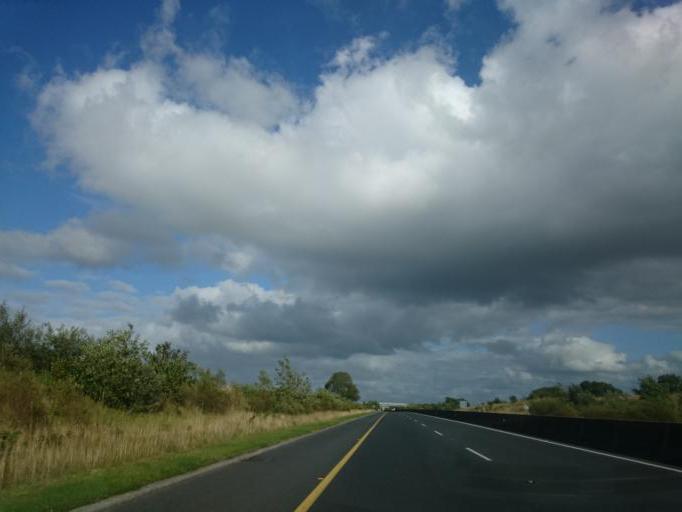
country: IE
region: Connaught
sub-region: County Galway
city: Athenry
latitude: 53.2746
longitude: -8.7043
